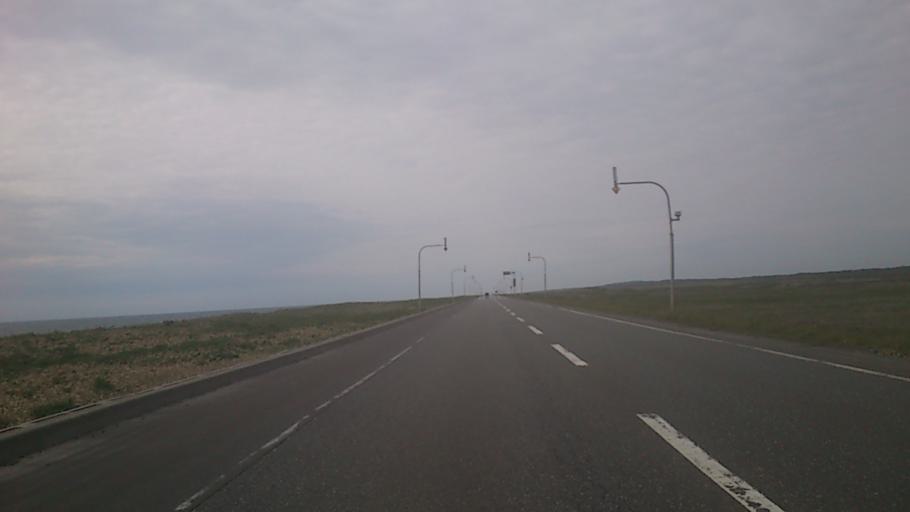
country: JP
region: Hokkaido
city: Makubetsu
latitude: 45.0252
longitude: 141.6682
